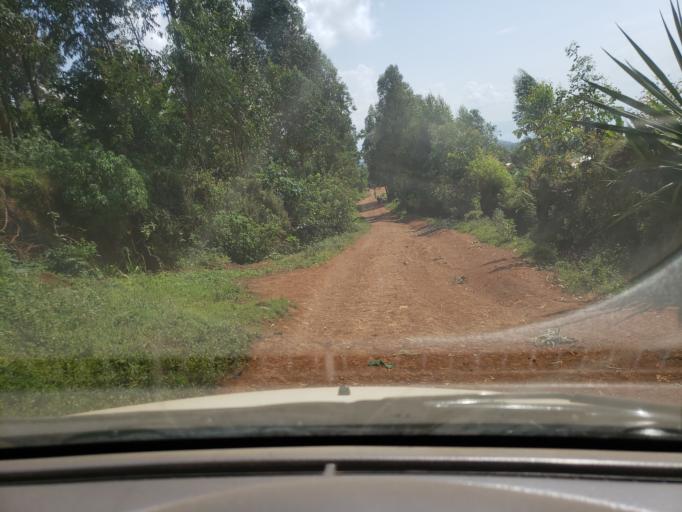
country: CD
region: South Kivu
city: Bukavu
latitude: -2.5066
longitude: 28.8252
